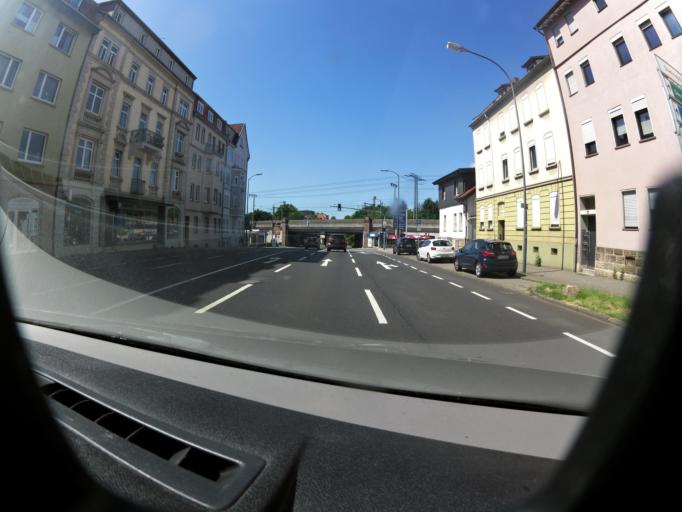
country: DE
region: Hesse
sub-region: Regierungsbezirk Kassel
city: Fulda
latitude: 50.5603
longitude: 9.6810
